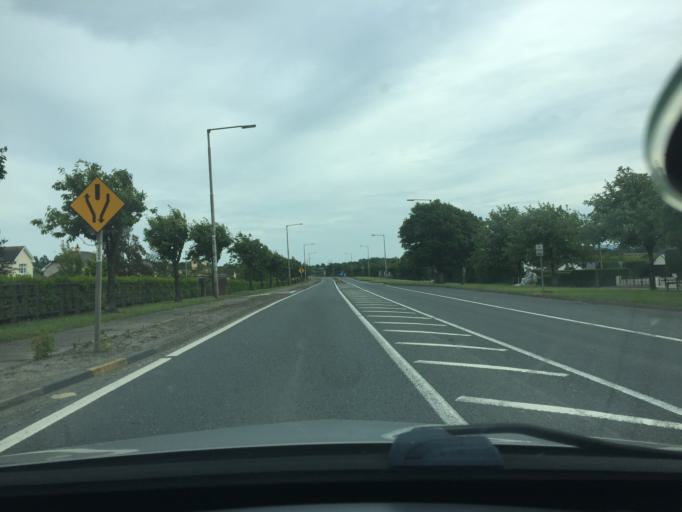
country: IE
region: Leinster
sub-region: Loch Garman
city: Enniscorthy
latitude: 52.4227
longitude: -6.5297
